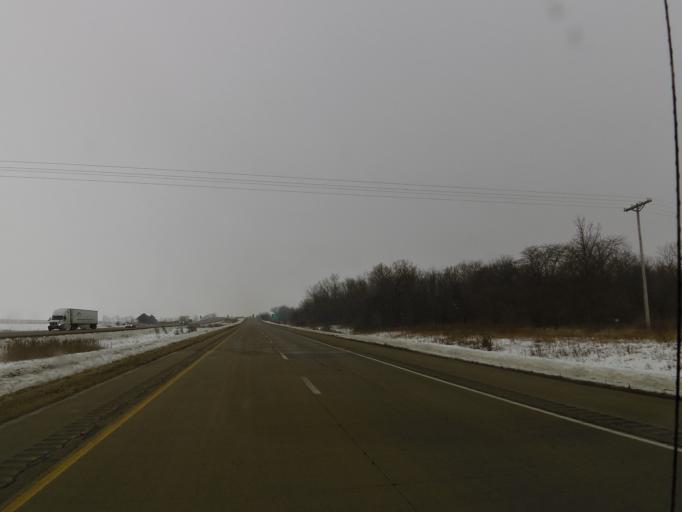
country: US
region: Illinois
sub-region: LaSalle County
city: Mendota
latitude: 41.4845
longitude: -89.0493
